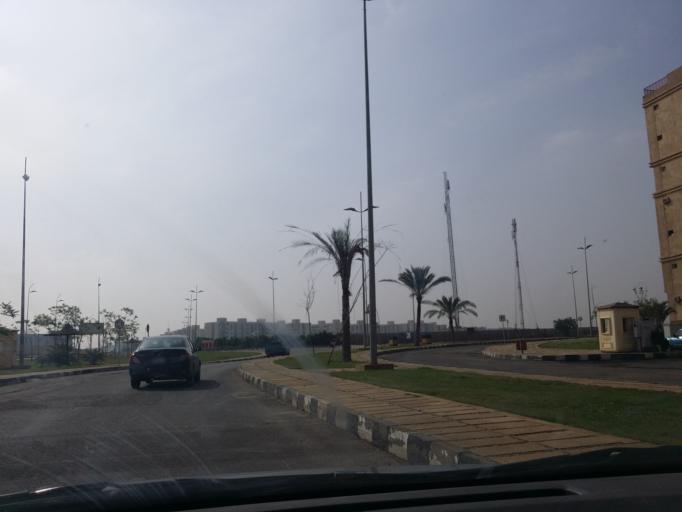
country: EG
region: Muhafazat al Qalyubiyah
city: Al Khankah
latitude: 30.0826
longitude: 31.6491
